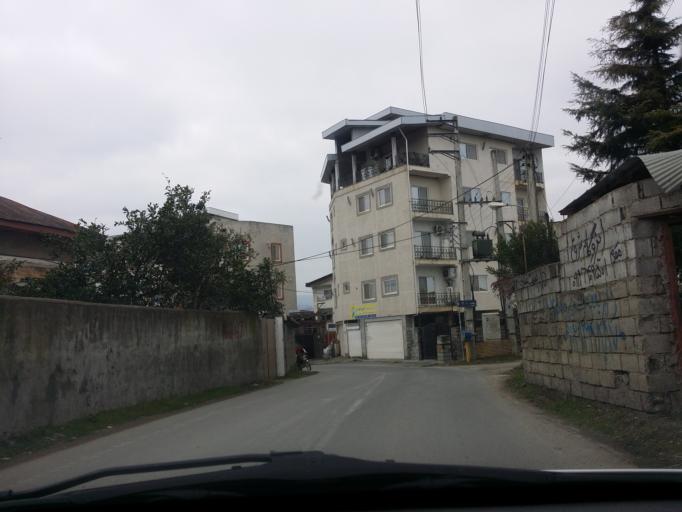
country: IR
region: Mazandaran
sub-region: Nowshahr
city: Nowshahr
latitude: 36.6453
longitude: 51.4822
